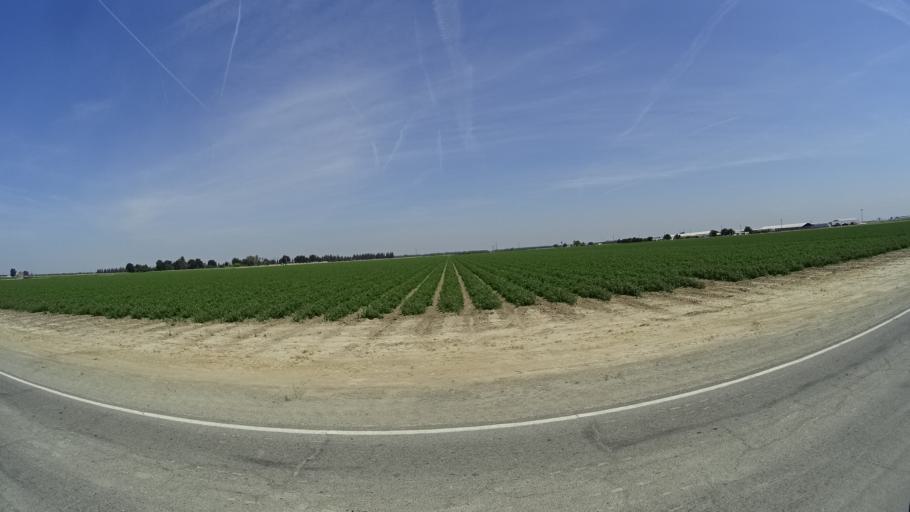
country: US
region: California
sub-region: Kings County
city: Lucerne
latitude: 36.4014
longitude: -119.5685
